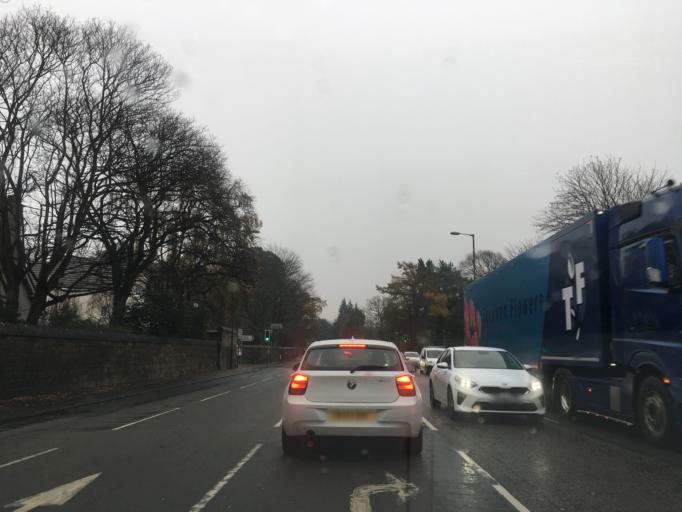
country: GB
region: Scotland
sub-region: Edinburgh
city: Currie
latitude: 55.9605
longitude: -3.3021
